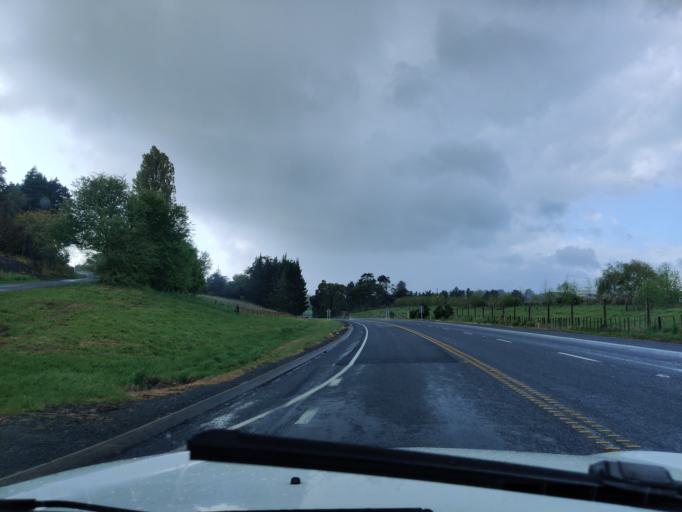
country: NZ
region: Waikato
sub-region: Waipa District
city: Cambridge
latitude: -37.9393
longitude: 175.5775
